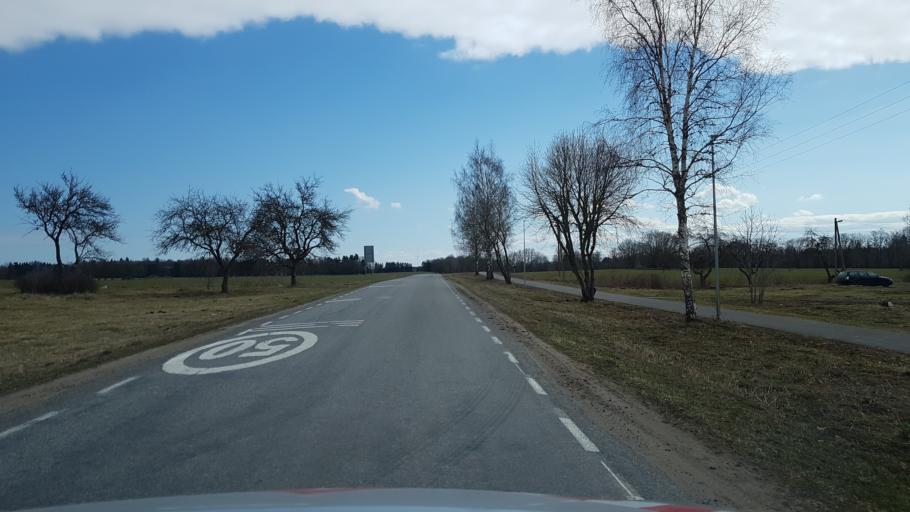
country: EE
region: Laeaene-Virumaa
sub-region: Haljala vald
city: Haljala
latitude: 59.3982
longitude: 26.2757
